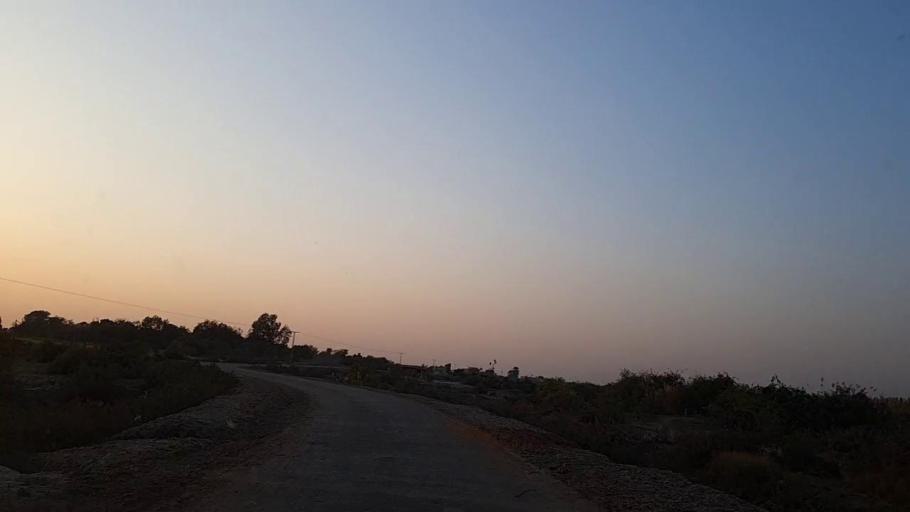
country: PK
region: Sindh
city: Bhit Shah
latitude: 25.9236
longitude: 68.4889
